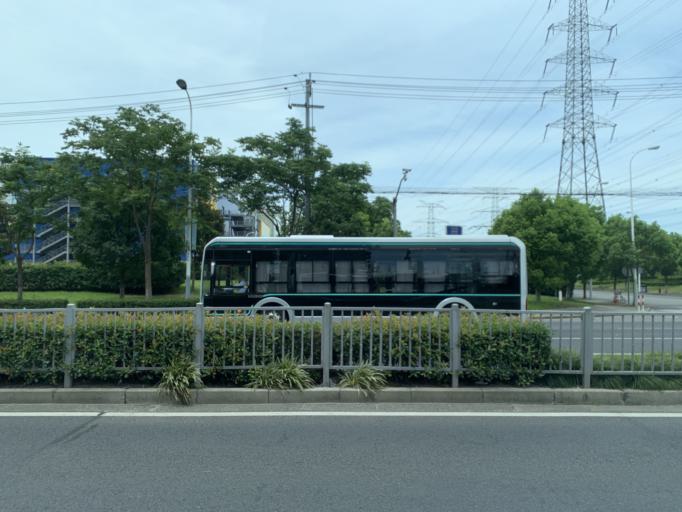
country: CN
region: Shanghai Shi
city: Kangqiao
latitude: 31.1629
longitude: 121.5595
